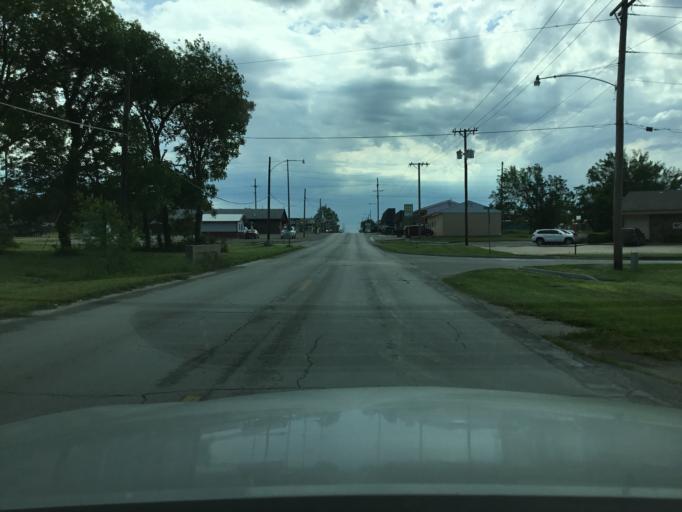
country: US
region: Kansas
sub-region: Montgomery County
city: Coffeyville
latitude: 37.0363
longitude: -95.6448
